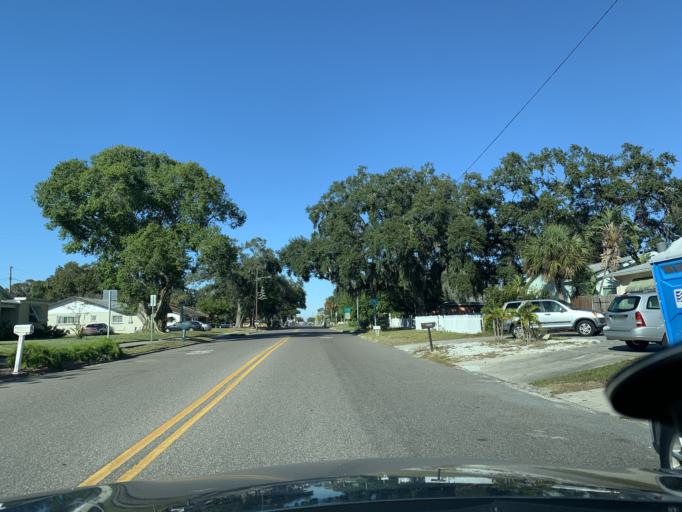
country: US
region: Florida
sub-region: Pinellas County
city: Gulfport
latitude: 27.7442
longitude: -82.6997
